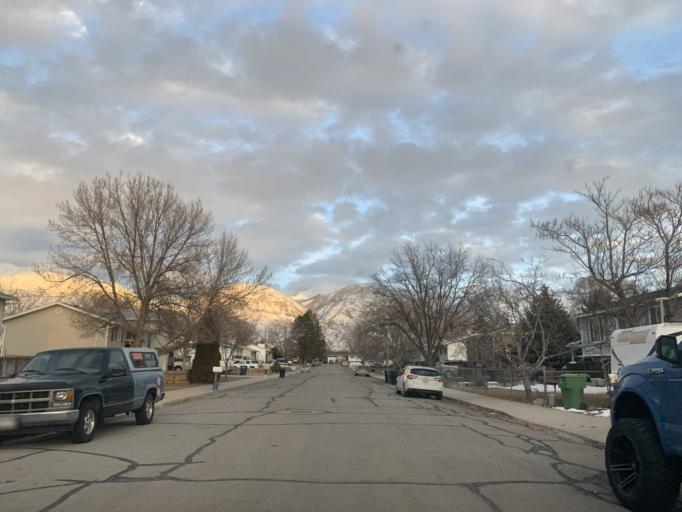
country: US
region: Utah
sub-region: Utah County
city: Provo
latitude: 40.2434
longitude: -111.7007
